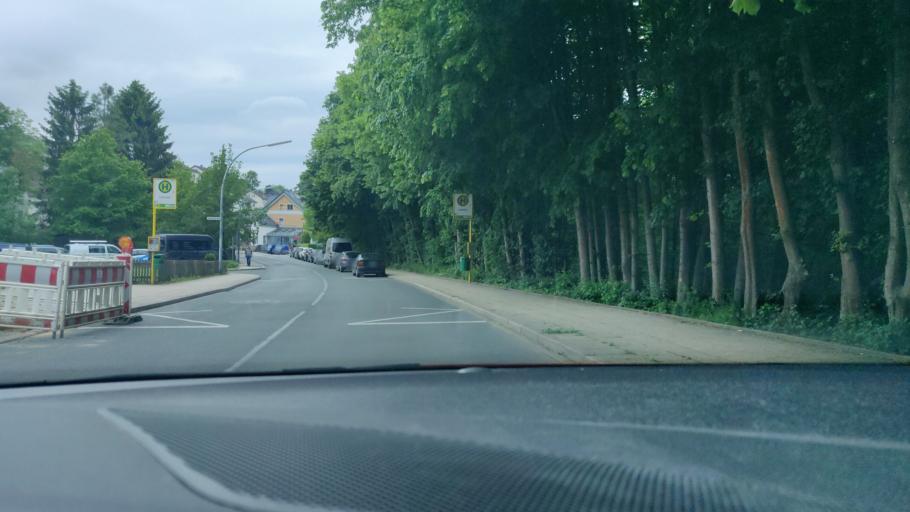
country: DE
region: North Rhine-Westphalia
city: Wulfrath
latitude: 51.3024
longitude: 7.0925
